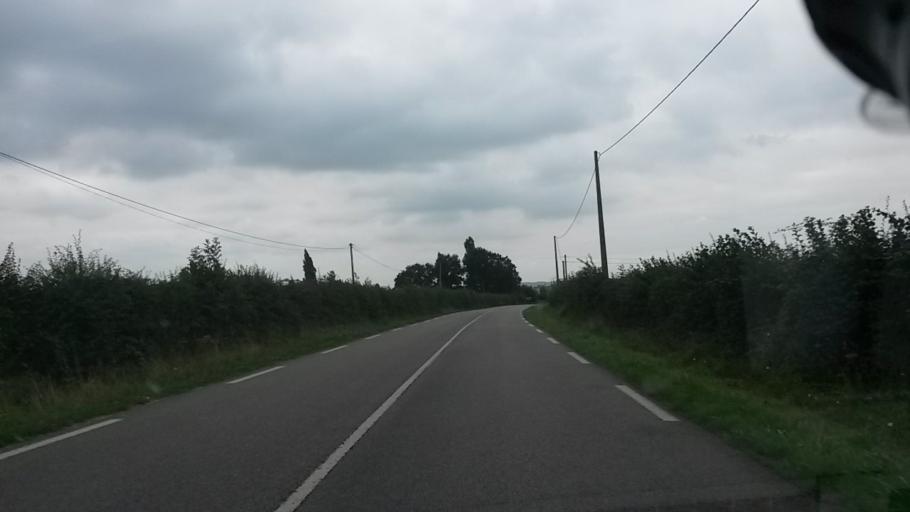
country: FR
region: Haute-Normandie
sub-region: Departement de la Seine-Maritime
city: Forges-les-Eaux
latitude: 49.6240
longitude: 1.5698
